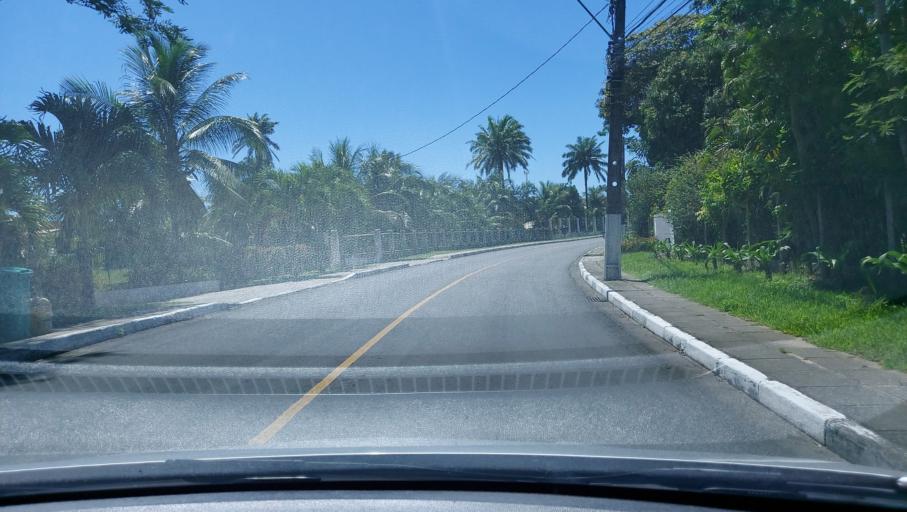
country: BR
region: Bahia
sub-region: Lauro De Freitas
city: Lauro de Freitas
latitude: -12.8683
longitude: -38.3069
